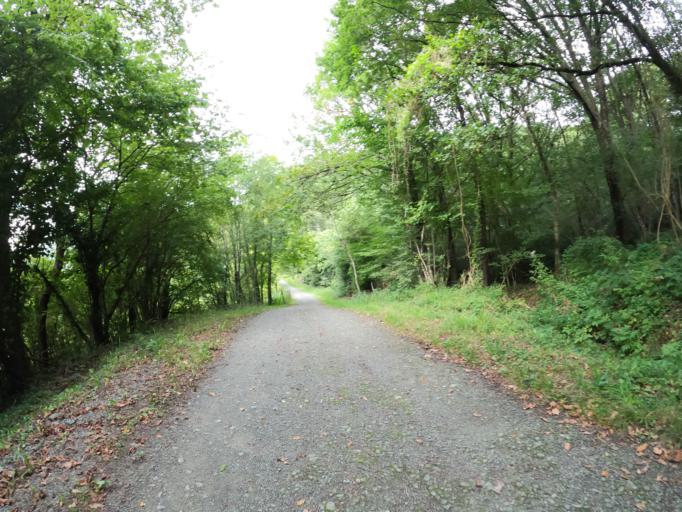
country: ES
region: Navarre
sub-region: Provincia de Navarra
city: Lekunberri
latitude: 43.0130
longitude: -1.9002
